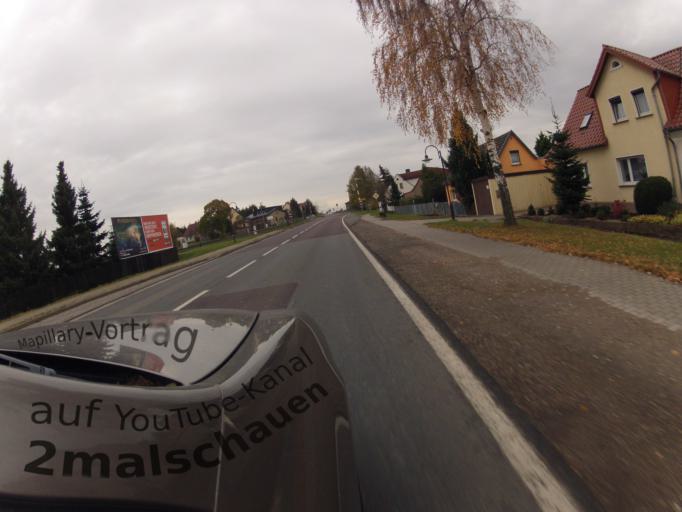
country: DE
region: Saxony-Anhalt
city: Peissen
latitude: 51.7183
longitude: 11.7585
